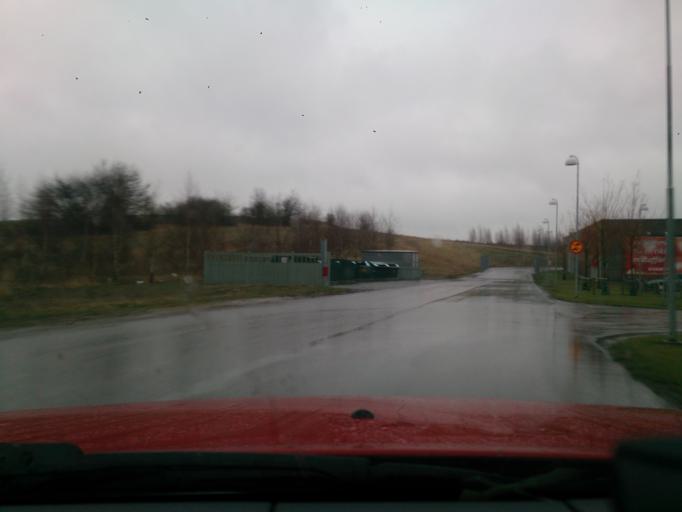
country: SE
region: Skane
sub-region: Ystads Kommun
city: Ystad
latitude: 55.4446
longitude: 13.8078
